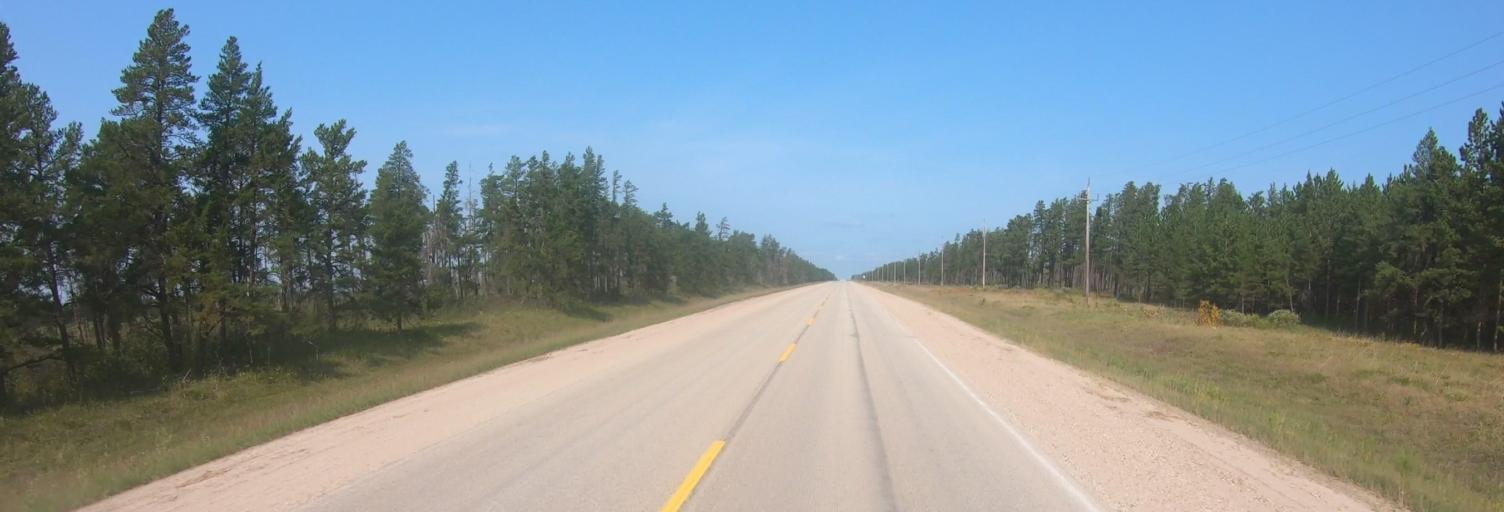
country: US
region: Minnesota
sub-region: Roseau County
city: Roseau
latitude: 49.1226
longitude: -96.0609
